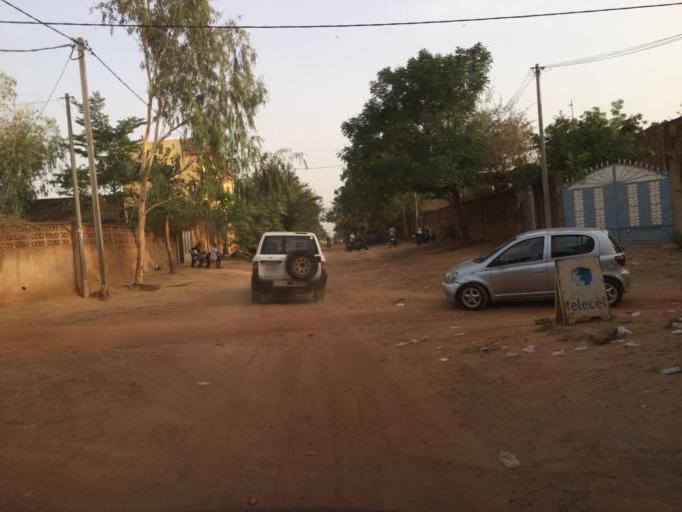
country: BF
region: Centre
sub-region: Kadiogo Province
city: Ouagadougou
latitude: 12.3669
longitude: -1.4990
